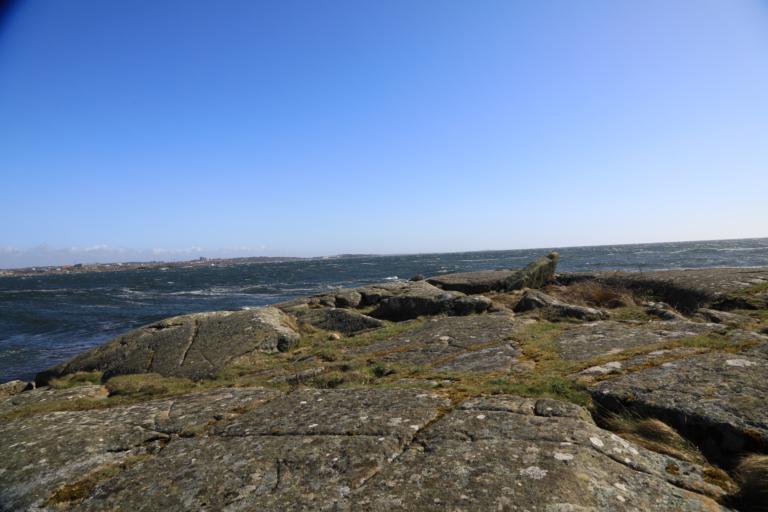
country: SE
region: Halland
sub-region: Varbergs Kommun
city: Varberg
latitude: 57.1151
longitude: 12.1960
